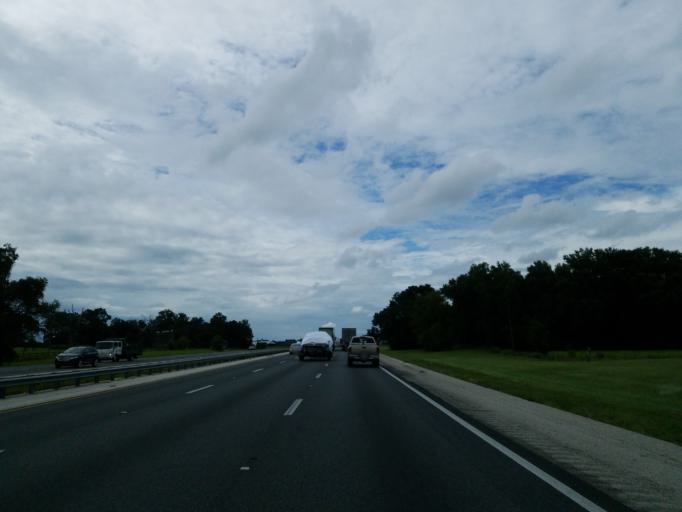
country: US
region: Florida
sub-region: Sumter County
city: Wildwood
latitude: 28.9019
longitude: -82.1045
